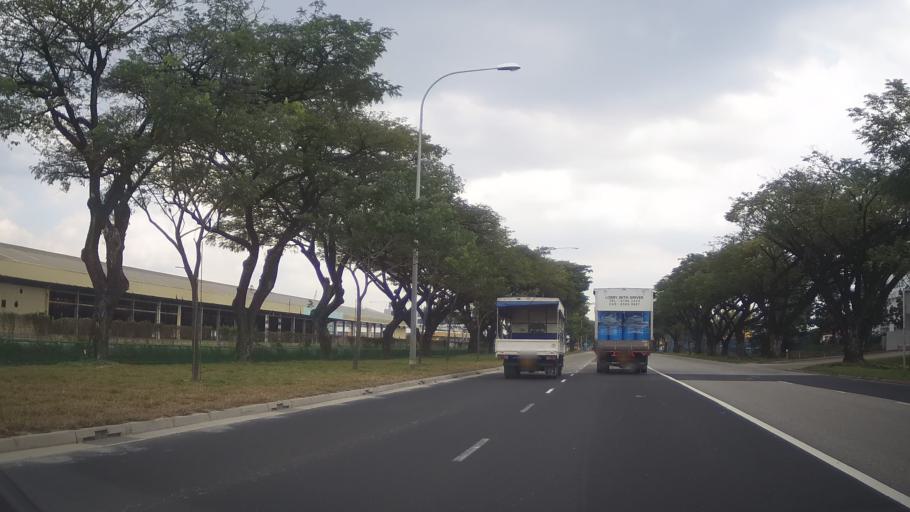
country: MY
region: Johor
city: Johor Bahru
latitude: 1.3081
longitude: 103.6660
